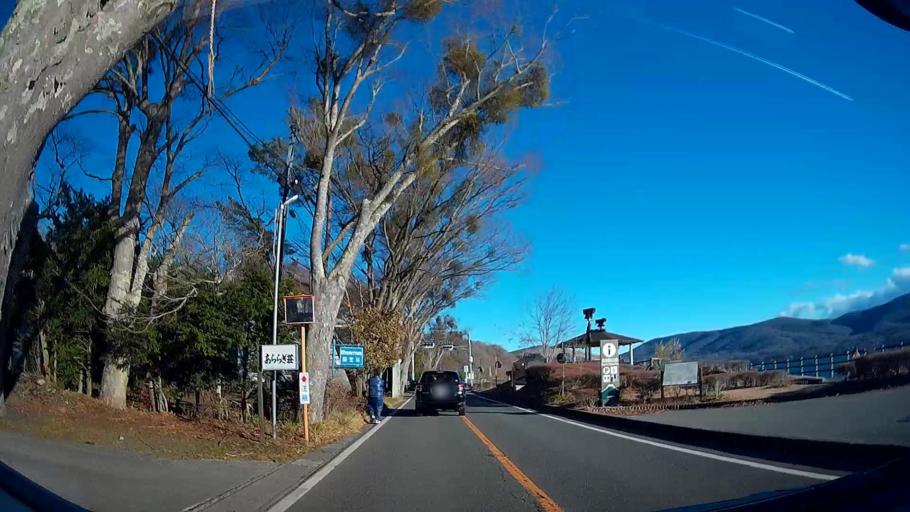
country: JP
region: Shizuoka
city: Gotemba
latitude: 35.4272
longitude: 138.8709
